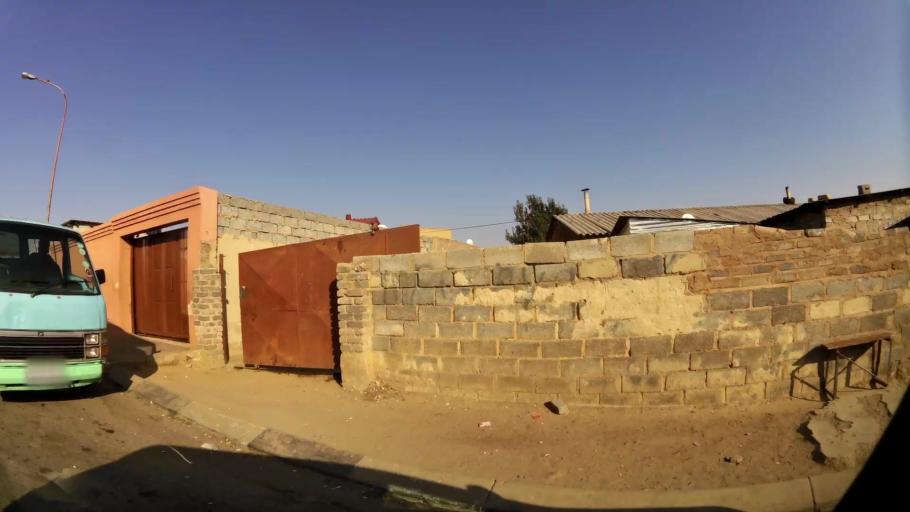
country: ZA
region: Gauteng
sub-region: City of Johannesburg Metropolitan Municipality
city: Soweto
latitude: -26.2588
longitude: 27.9486
